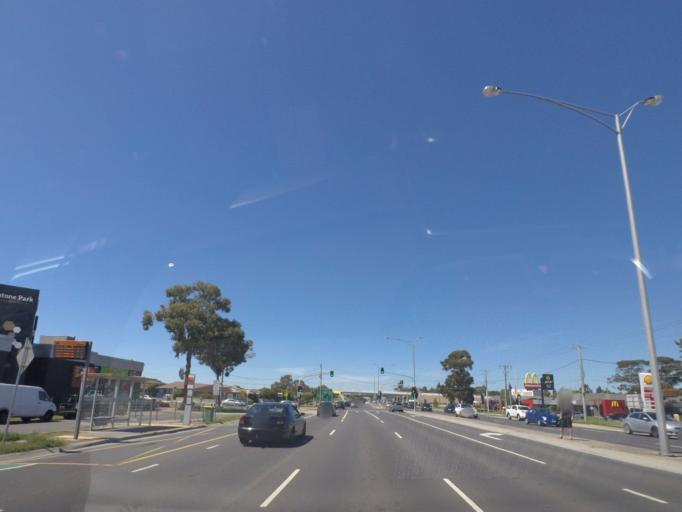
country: AU
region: Victoria
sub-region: Hume
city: Gladstone Park
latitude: -37.6874
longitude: 144.8826
